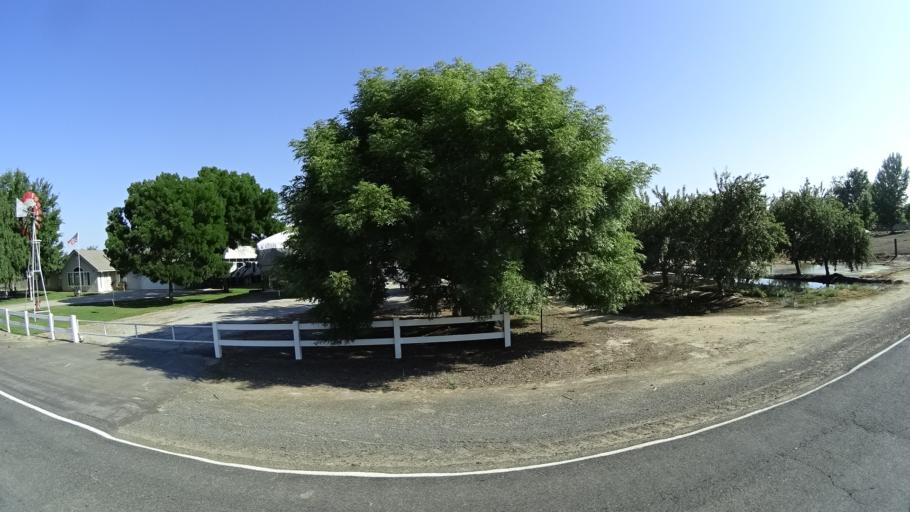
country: US
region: California
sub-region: Fresno County
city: Riverdale
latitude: 36.3658
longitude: -119.8315
